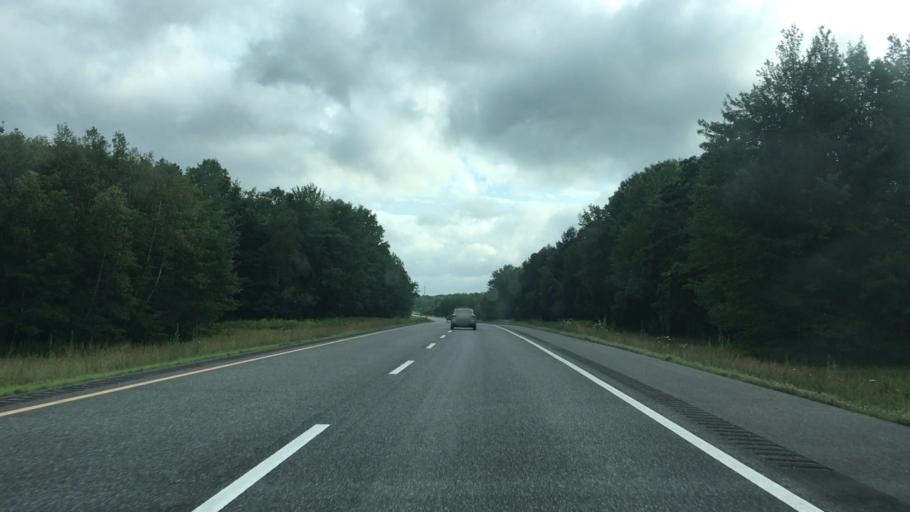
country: US
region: Maine
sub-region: Kennebec County
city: Clinton
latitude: 44.6488
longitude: -69.5183
